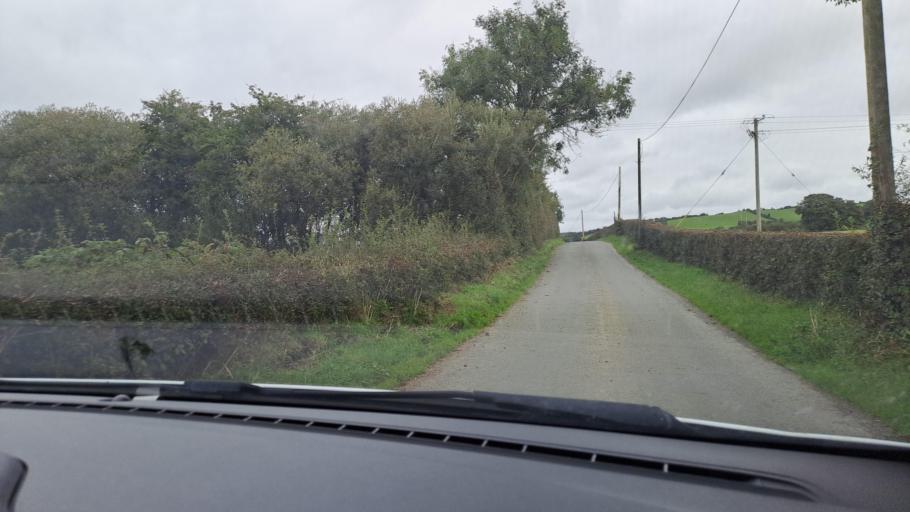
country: IE
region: Ulster
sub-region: An Cabhan
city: Kingscourt
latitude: 54.0210
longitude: -6.8273
